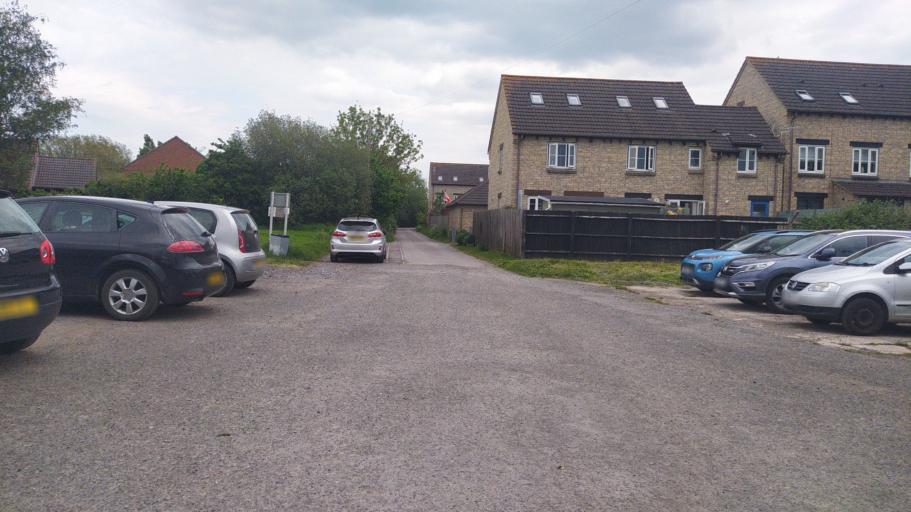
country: GB
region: England
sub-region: Wiltshire
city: Melksham
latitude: 51.3813
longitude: -2.1327
